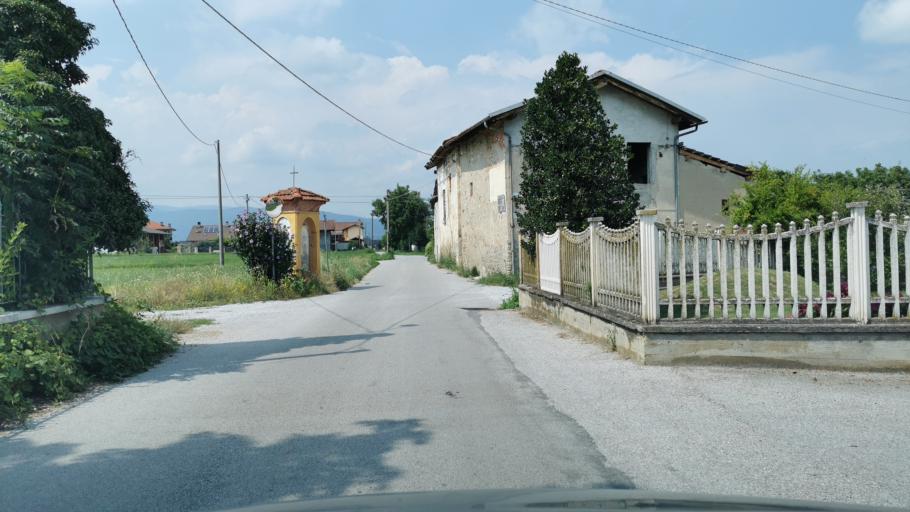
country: IT
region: Piedmont
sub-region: Provincia di Cuneo
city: Caraglio
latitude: 44.4259
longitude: 7.4524
